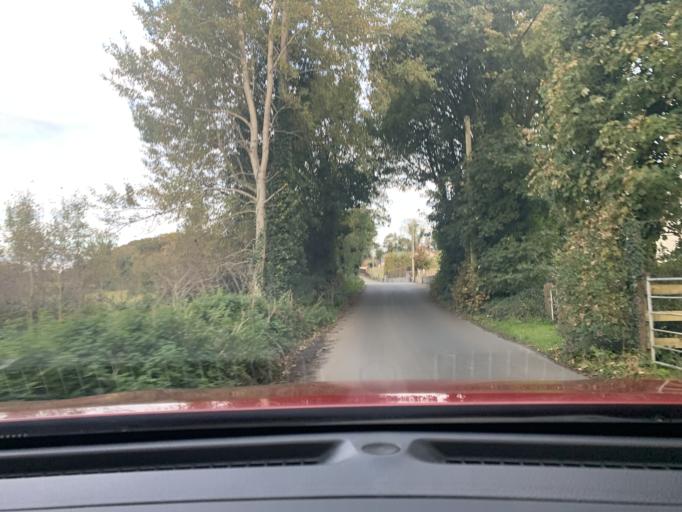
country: IE
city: Ballisodare
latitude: 54.2307
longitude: -8.5152
